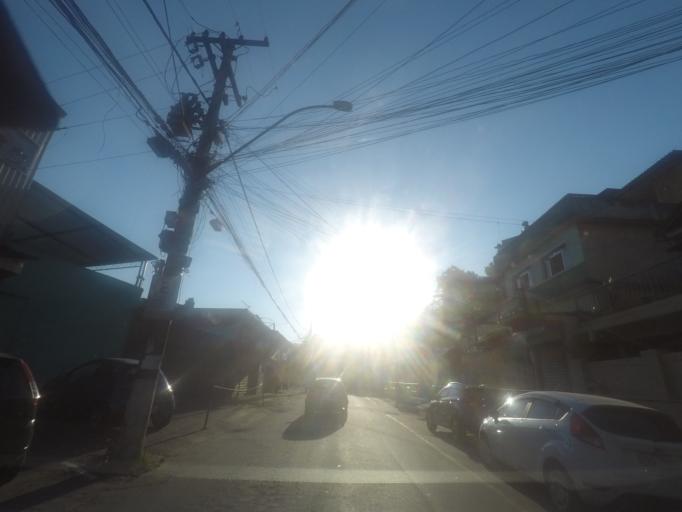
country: BR
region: Rio de Janeiro
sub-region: Petropolis
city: Petropolis
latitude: -22.5261
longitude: -43.1723
